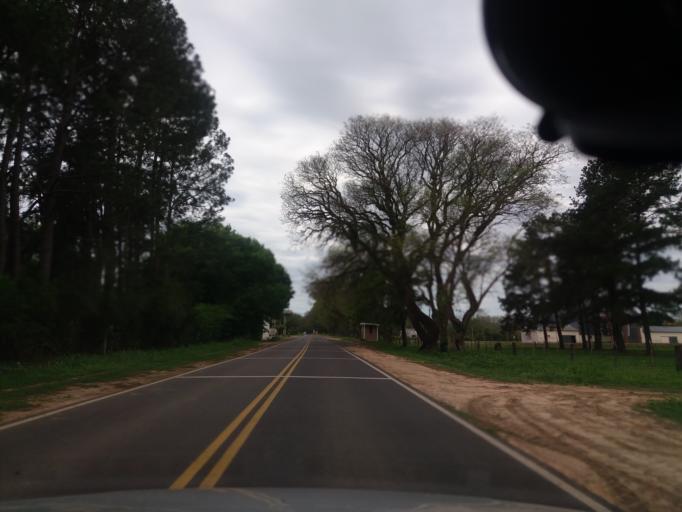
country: AR
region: Corrientes
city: Riachuelo
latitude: -27.4566
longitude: -58.6913
